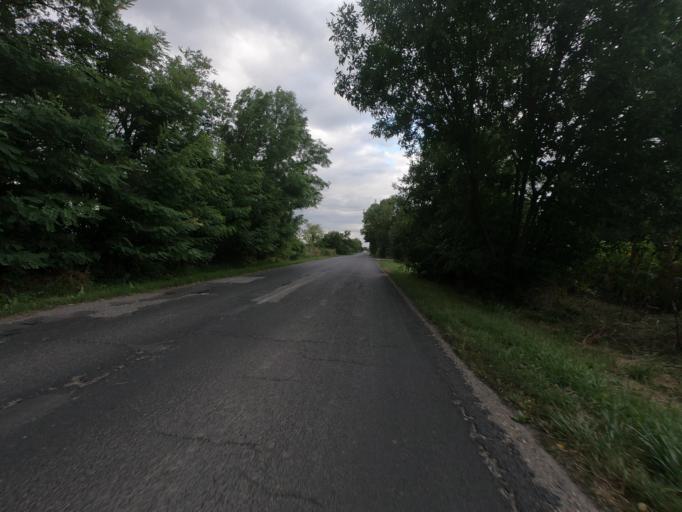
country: HU
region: Heves
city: Poroszlo
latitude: 47.6928
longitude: 20.6558
